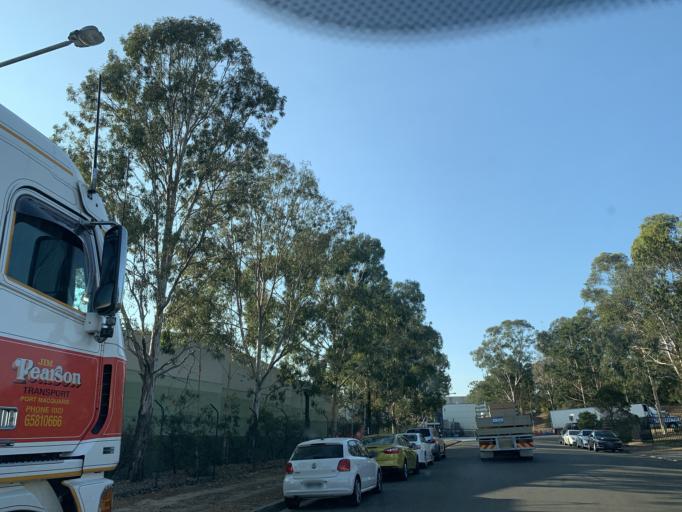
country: AU
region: New South Wales
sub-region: Blacktown
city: Doonside
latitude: -33.7964
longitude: 150.8768
